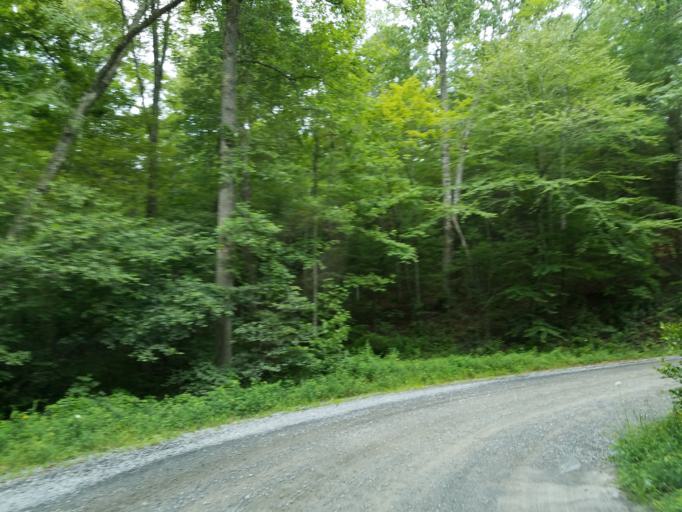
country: US
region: Georgia
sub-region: Fannin County
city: Blue Ridge
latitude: 34.8228
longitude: -84.2307
